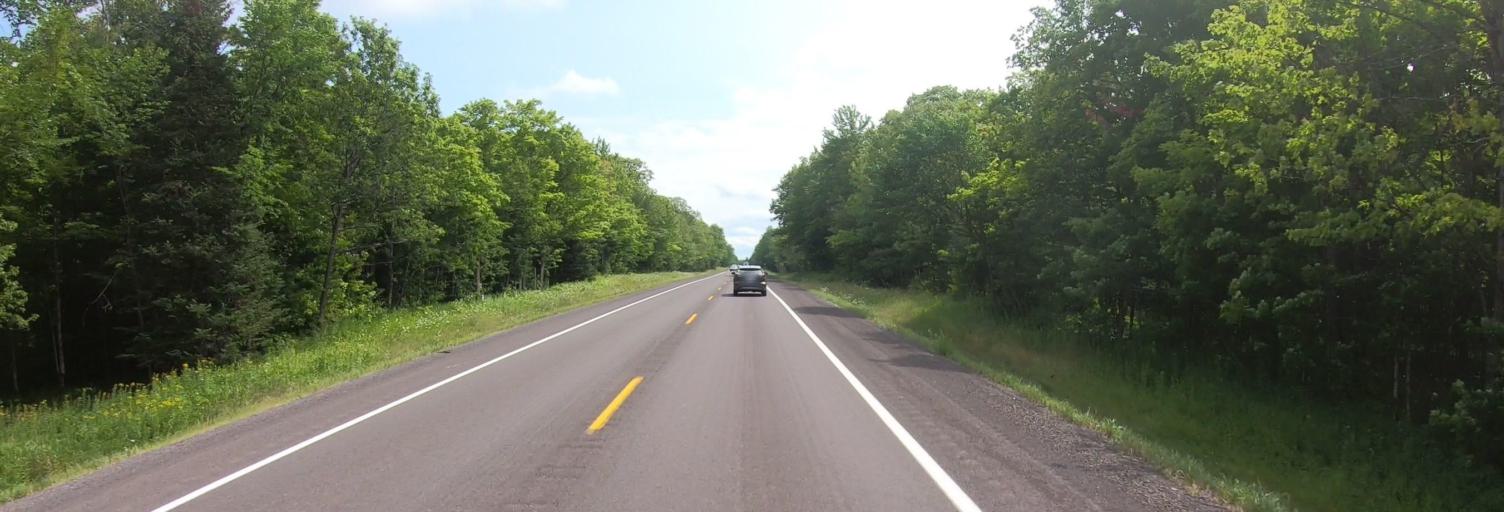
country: US
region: Michigan
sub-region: Houghton County
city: Hancock
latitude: 46.9835
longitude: -88.7810
